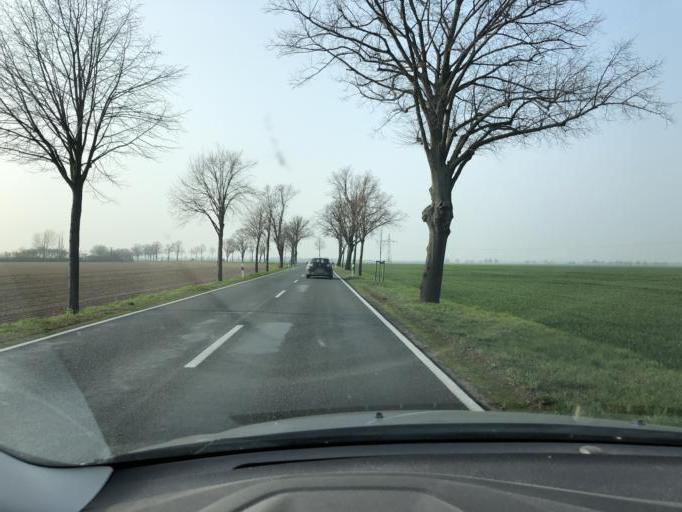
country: DE
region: Saxony-Anhalt
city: Roitzsch
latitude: 51.5395
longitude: 12.2727
